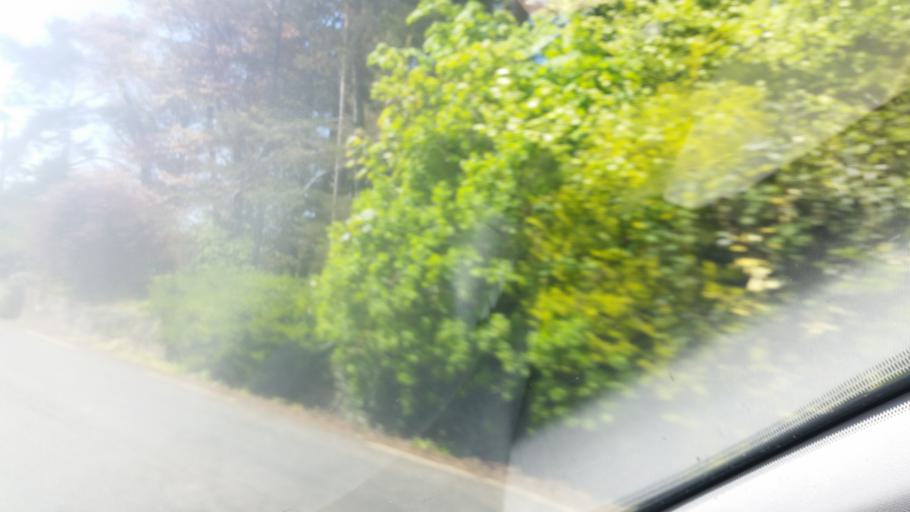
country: IE
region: Munster
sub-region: Waterford
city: Dunmore East
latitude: 52.2150
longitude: -6.8588
